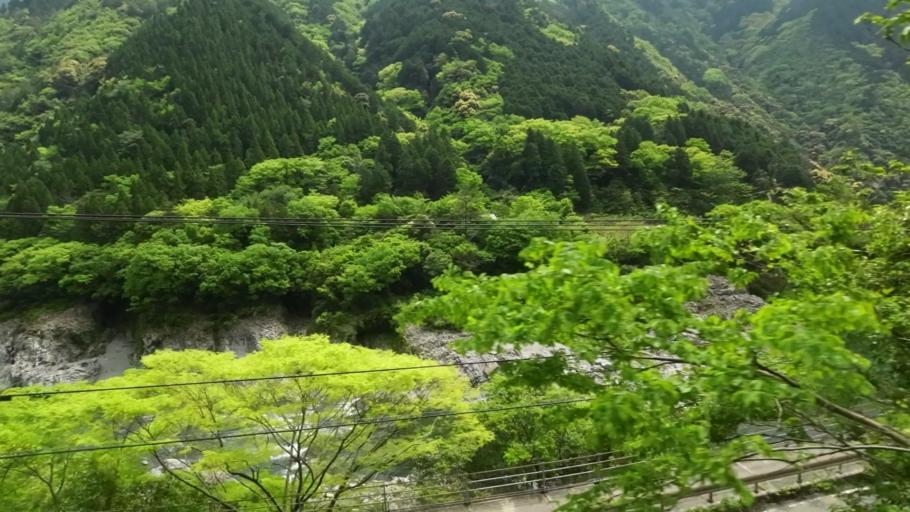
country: JP
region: Tokushima
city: Ikedacho
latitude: 33.9176
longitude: 133.7565
